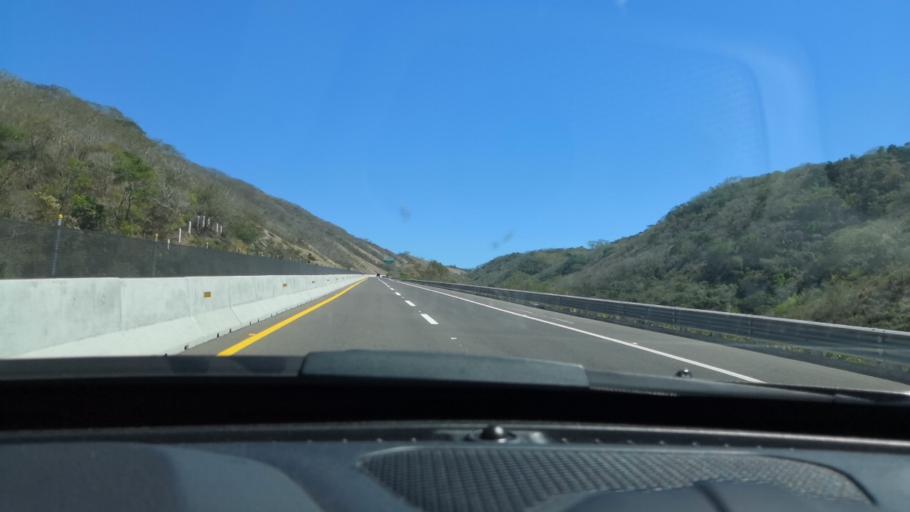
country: MX
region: Nayarit
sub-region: Compostela
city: Juan Escutia (Borbollon)
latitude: 21.1307
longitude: -104.9030
